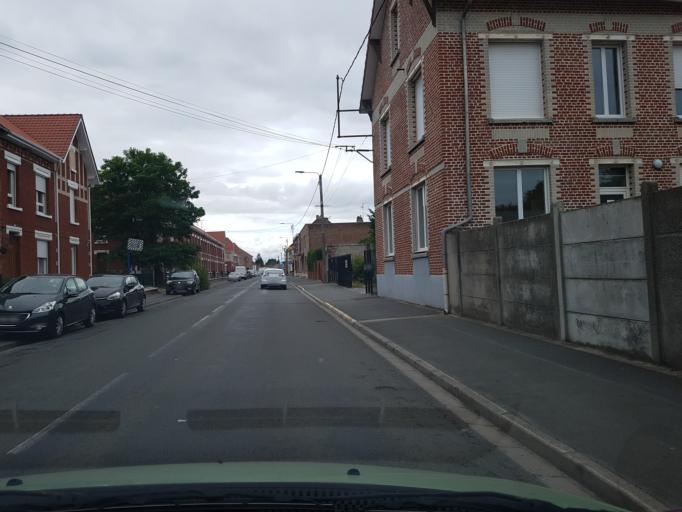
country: FR
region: Nord-Pas-de-Calais
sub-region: Departement du Pas-de-Calais
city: Wingles
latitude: 50.4971
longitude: 2.8710
